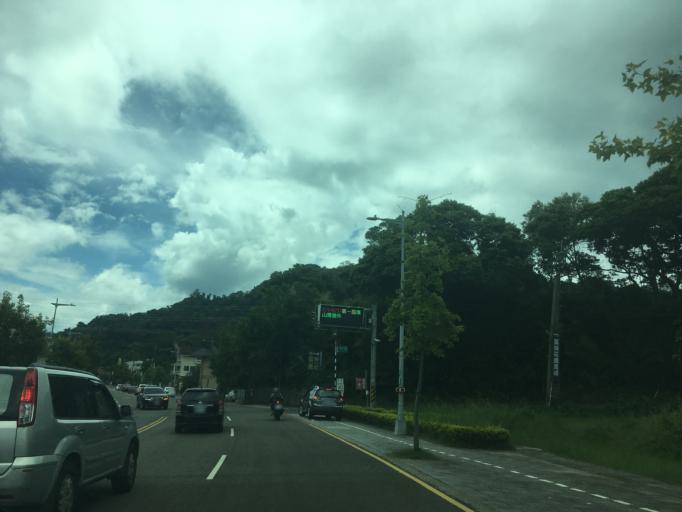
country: TW
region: Taiwan
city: Daxi
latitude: 24.8418
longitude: 121.2881
